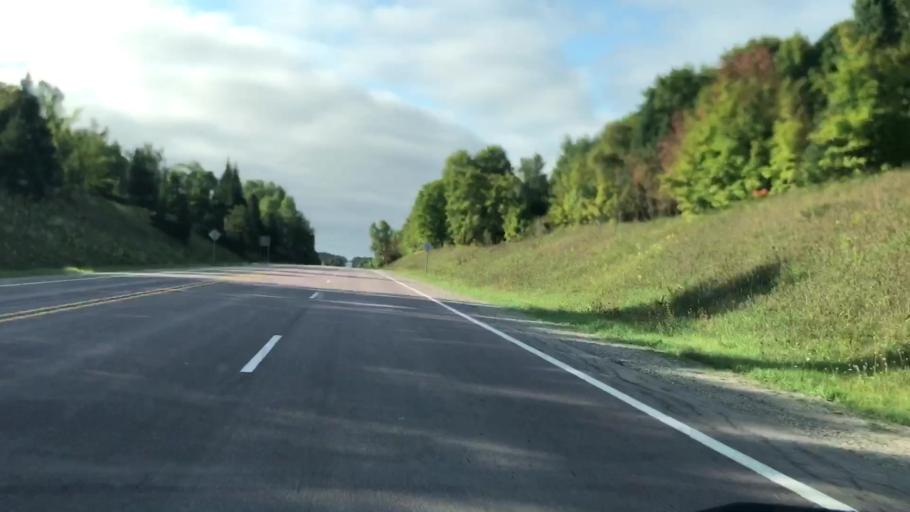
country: US
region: Michigan
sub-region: Luce County
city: Newberry
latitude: 46.3077
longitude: -85.5675
